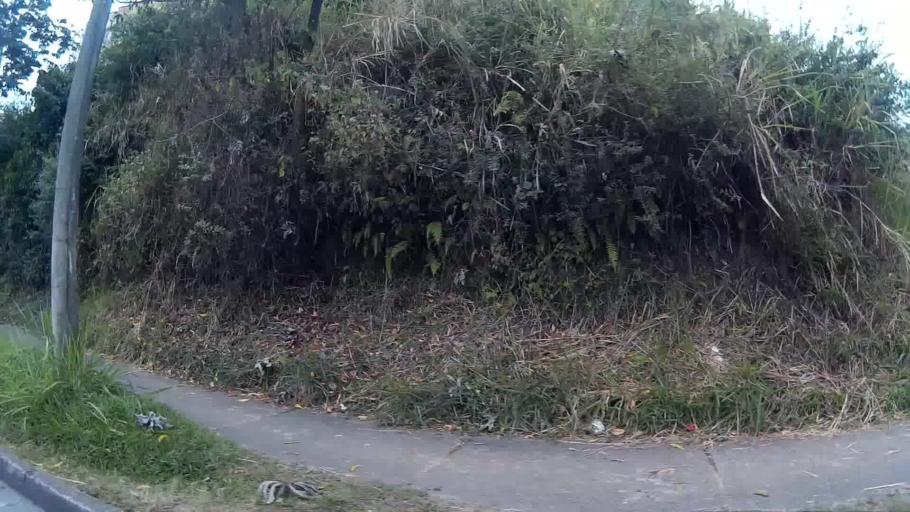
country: CO
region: Risaralda
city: Pereira
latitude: 4.8106
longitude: -75.7332
